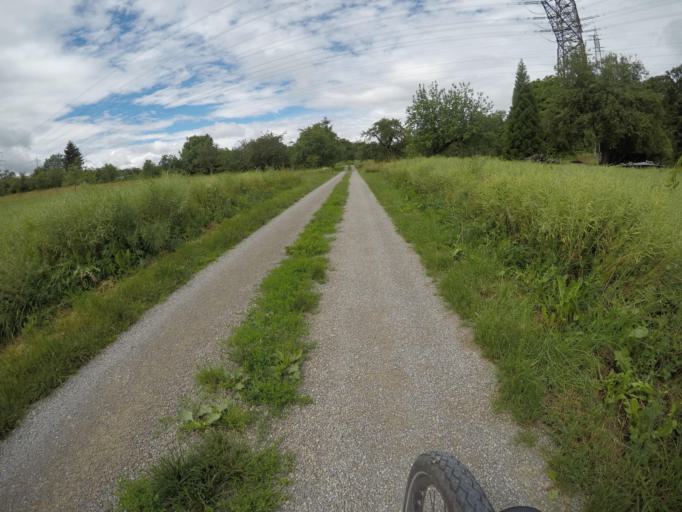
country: DE
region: Baden-Wuerttemberg
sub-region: Regierungsbezirk Stuttgart
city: Gartringen
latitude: 48.6477
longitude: 8.8728
